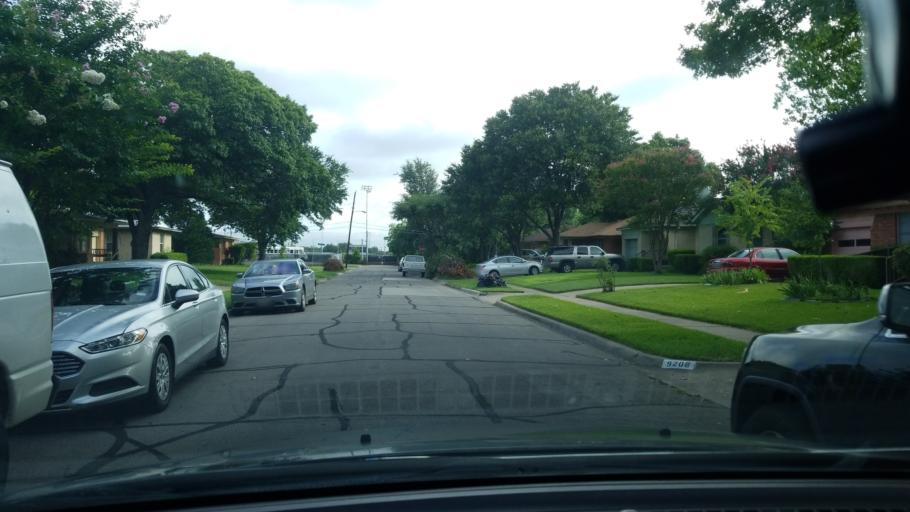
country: US
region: Texas
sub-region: Dallas County
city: Mesquite
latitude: 32.8166
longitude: -96.6787
